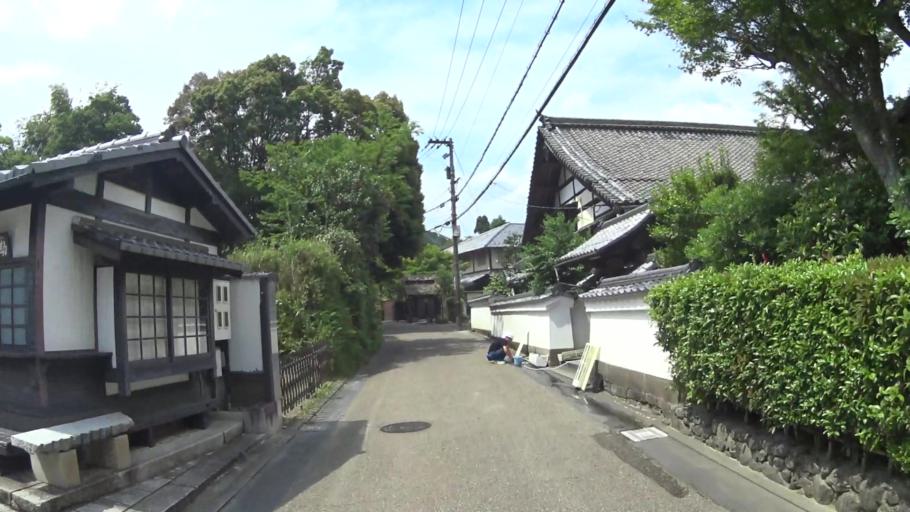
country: JP
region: Kyoto
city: Muko
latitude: 35.0235
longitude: 135.6686
